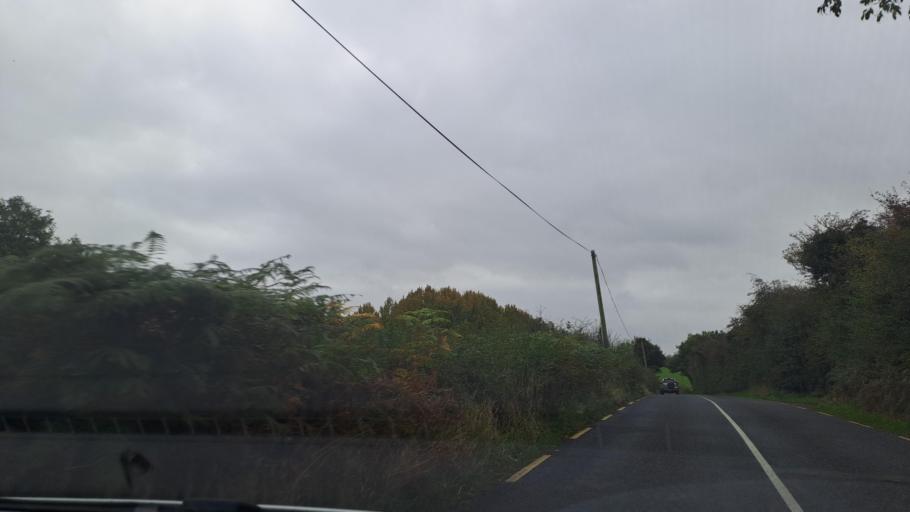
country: IE
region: Ulster
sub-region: An Cabhan
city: Cootehill
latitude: 54.0295
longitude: -7.0441
